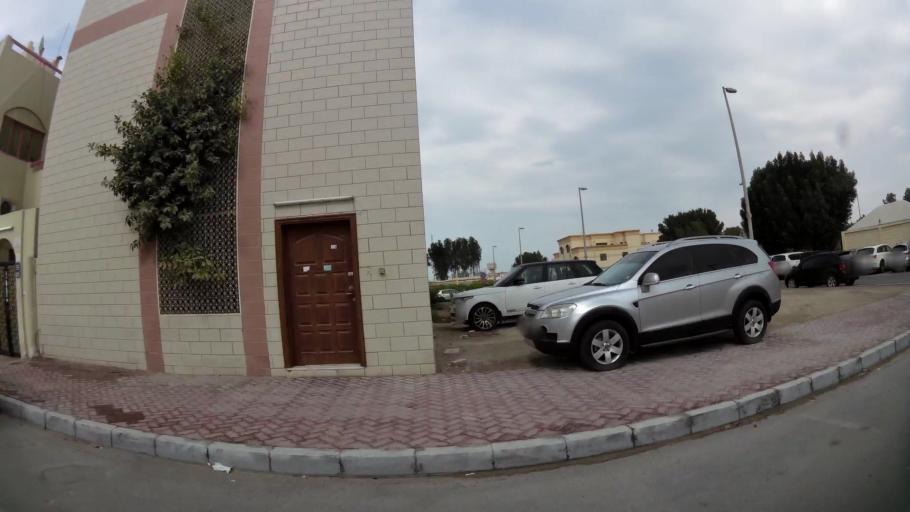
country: AE
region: Abu Dhabi
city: Abu Dhabi
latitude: 24.4283
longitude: 54.4045
